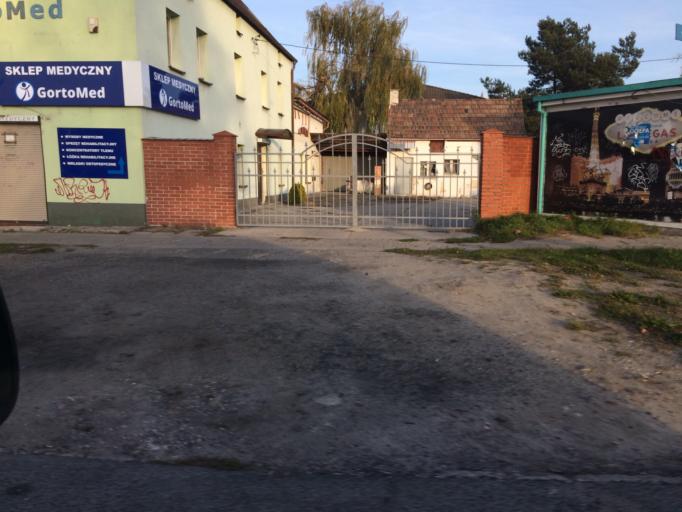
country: PL
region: Opole Voivodeship
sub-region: Powiat opolski
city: Opole
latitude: 50.6703
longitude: 17.9757
